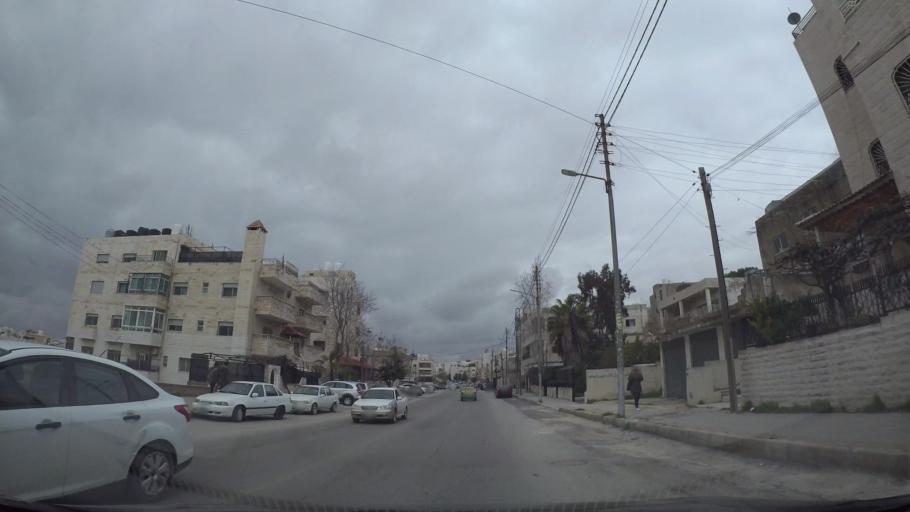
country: JO
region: Amman
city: Wadi as Sir
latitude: 31.9574
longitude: 35.8351
